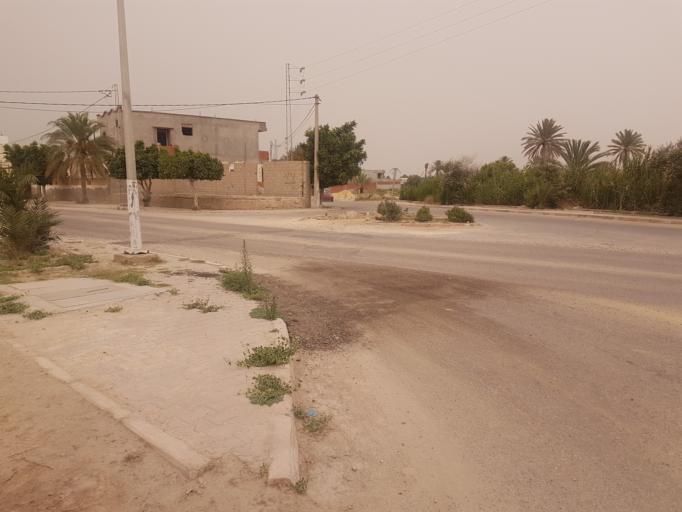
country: TN
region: Qabis
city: Gabes
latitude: 33.8864
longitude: 10.0676
